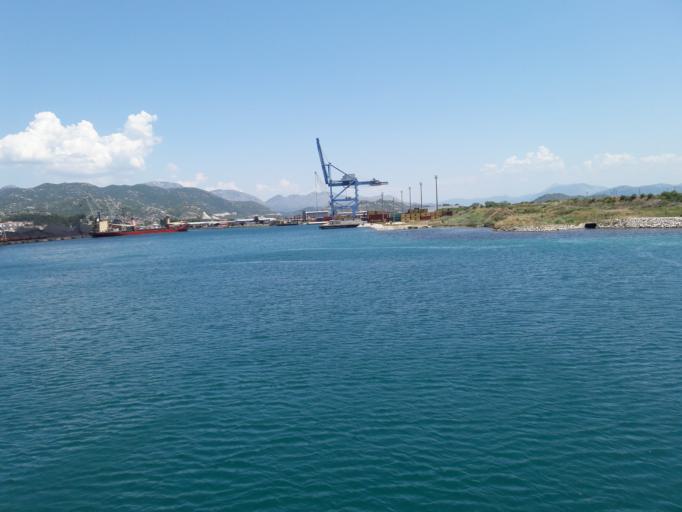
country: HR
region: Dubrovacko-Neretvanska
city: Komin
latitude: 43.0437
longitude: 17.4209
